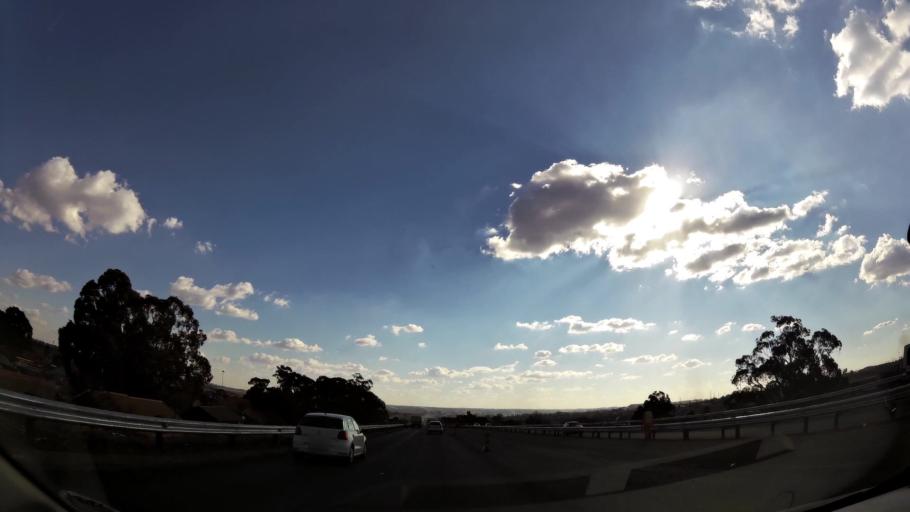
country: ZA
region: Mpumalanga
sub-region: Nkangala District Municipality
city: Witbank
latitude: -25.8831
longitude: 29.1902
